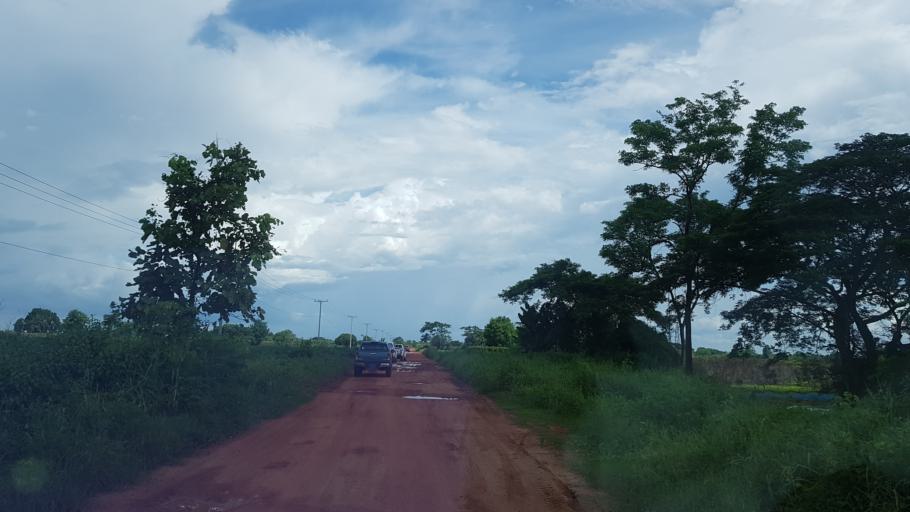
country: LA
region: Vientiane
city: Vientiane
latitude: 18.2324
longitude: 102.5633
